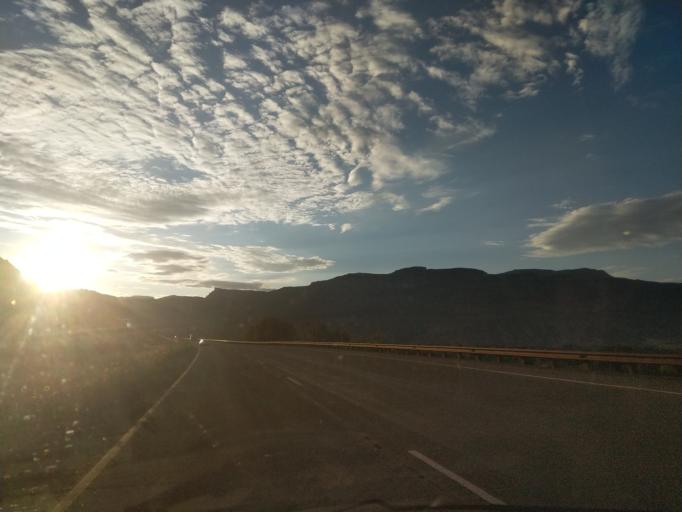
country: US
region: Colorado
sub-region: Mesa County
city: Palisade
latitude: 39.1167
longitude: -108.3529
